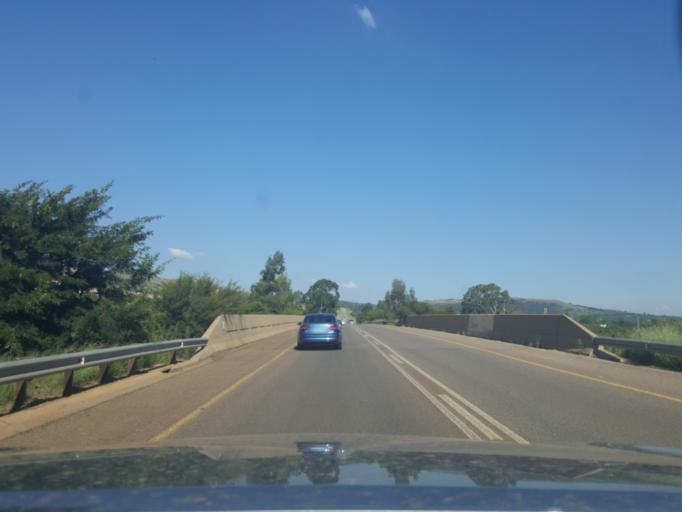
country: ZA
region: Gauteng
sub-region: City of Tshwane Metropolitan Municipality
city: Cullinan
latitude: -25.7689
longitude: 28.4388
